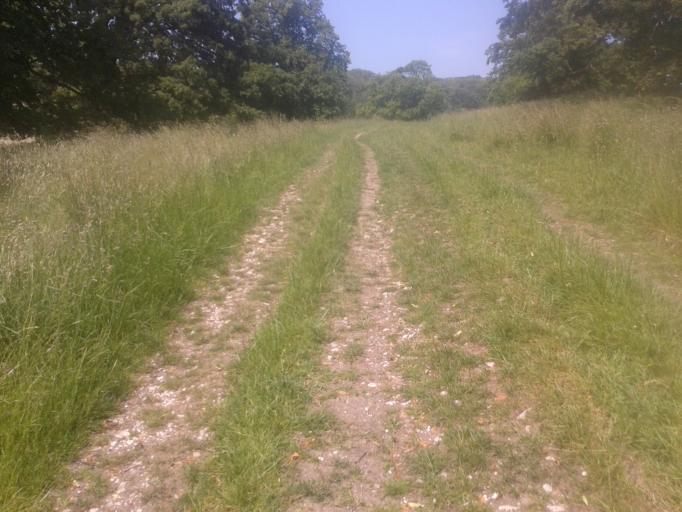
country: GB
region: England
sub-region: East Riding of Yorkshire
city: Londesborough
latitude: 53.8956
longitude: -0.6733
